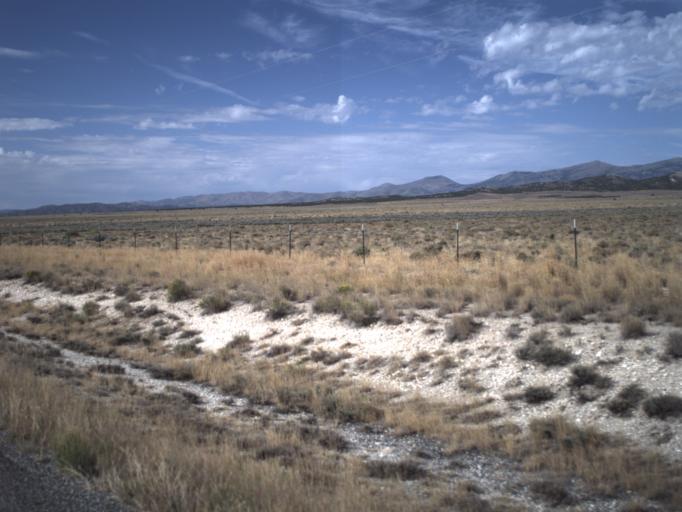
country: US
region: Idaho
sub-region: Cassia County
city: Burley
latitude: 41.7593
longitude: -113.5128
